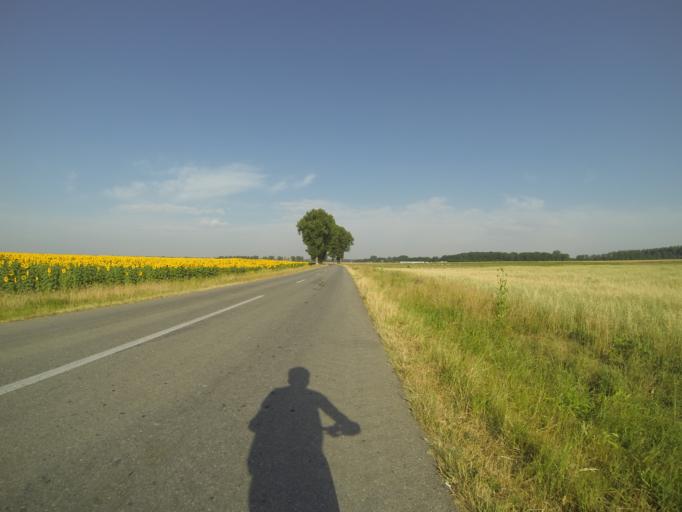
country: RO
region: Dolj
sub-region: Comuna Valea Stanciului
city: Valea Stanciului
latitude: 43.9818
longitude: 23.9086
